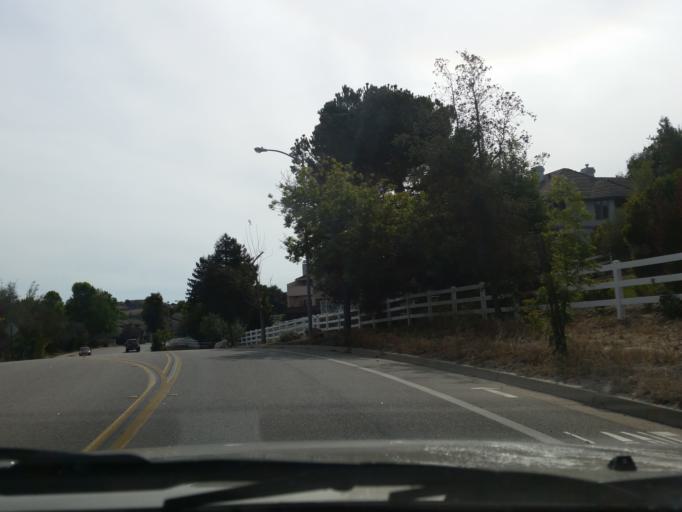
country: US
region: California
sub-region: San Luis Obispo County
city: Arroyo Grande
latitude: 35.1339
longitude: -120.5987
